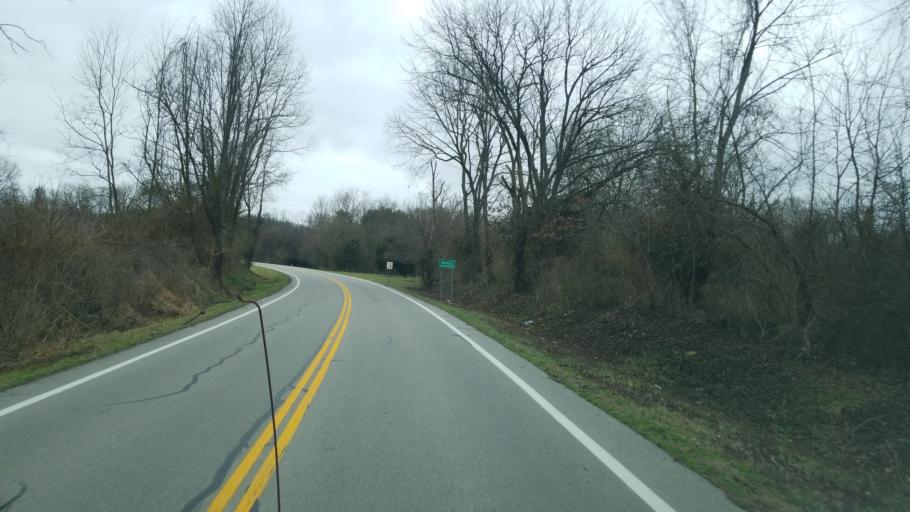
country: US
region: Ohio
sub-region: Clermont County
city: New Richmond
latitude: 38.8138
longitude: -84.2166
